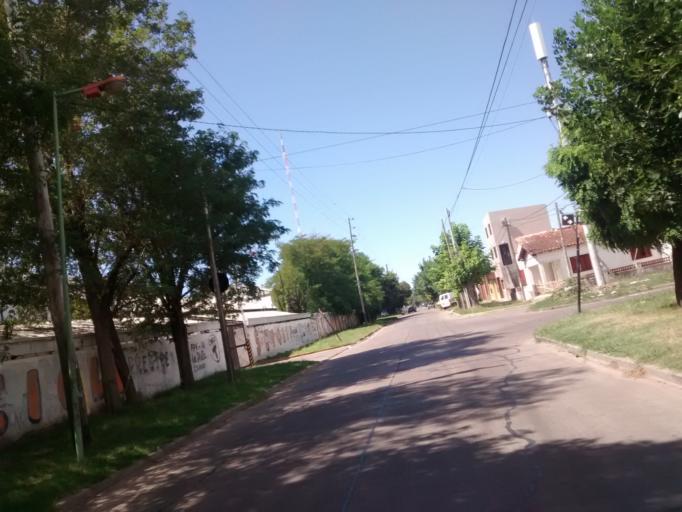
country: AR
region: Buenos Aires
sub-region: Partido de La Plata
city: La Plata
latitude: -34.9462
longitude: -57.9776
